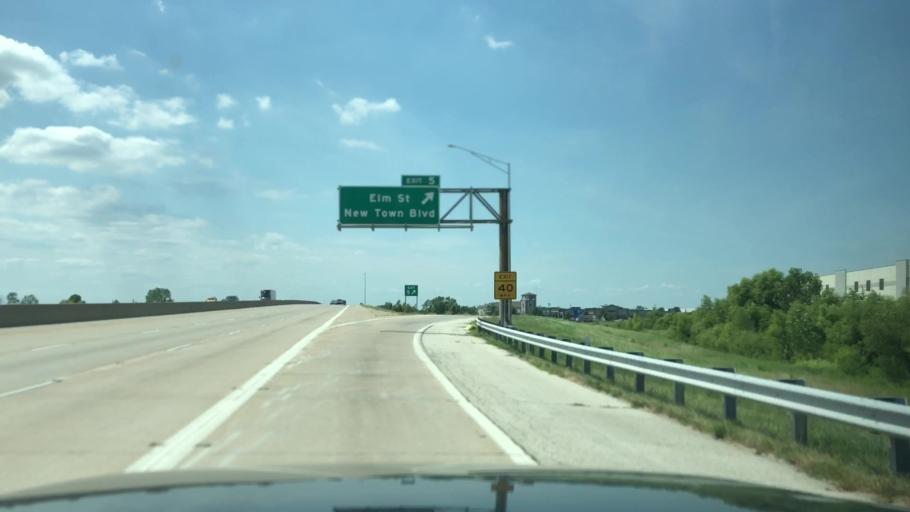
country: US
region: Missouri
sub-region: Saint Charles County
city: Saint Charles
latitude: 38.8234
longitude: -90.5141
